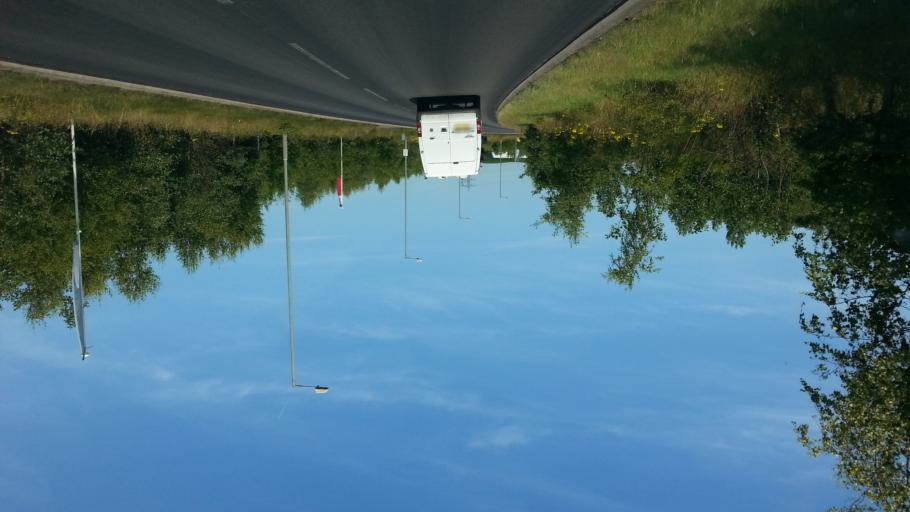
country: GB
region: England
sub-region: Staffordshire
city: Burntwood
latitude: 52.6737
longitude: -1.9428
